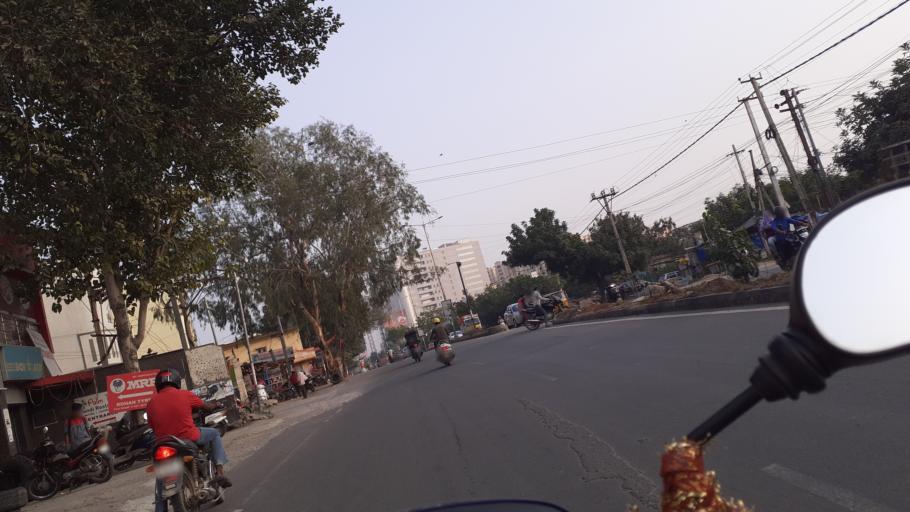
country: IN
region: Telangana
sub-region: Medak
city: Serilingampalle
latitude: 17.4884
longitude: 78.3553
